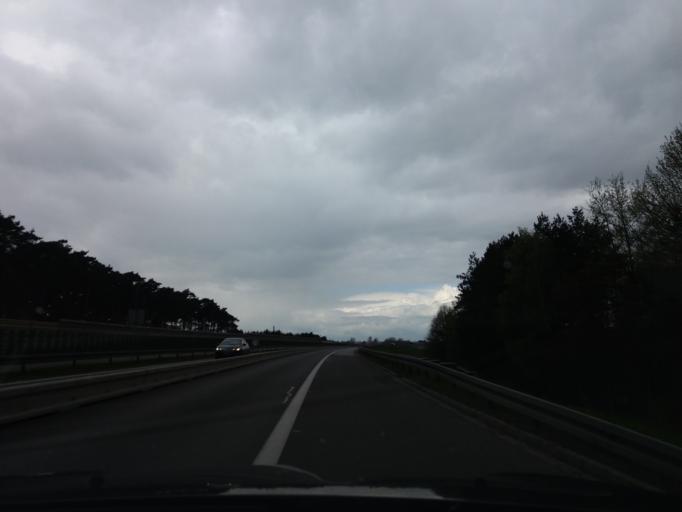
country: PL
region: Opole Voivodeship
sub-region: Powiat krapkowicki
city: Krapkowice
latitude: 50.4938
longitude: 17.9769
